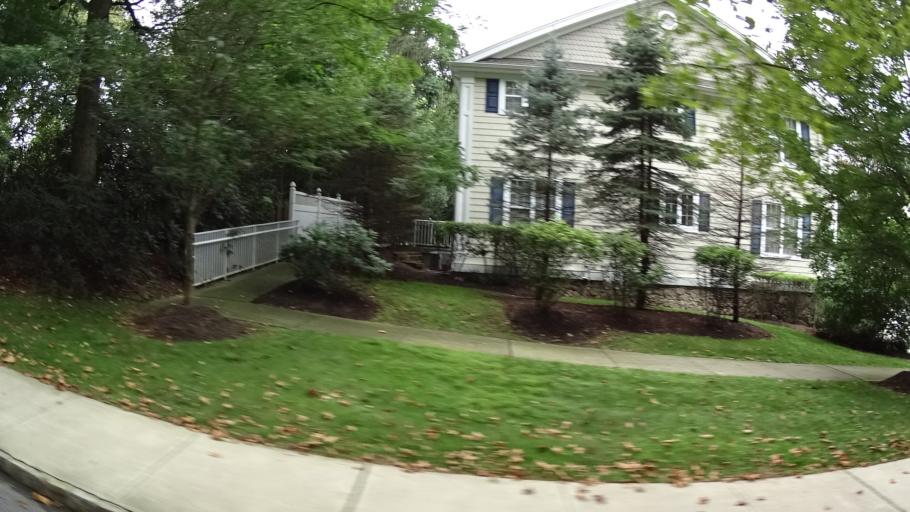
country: US
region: New Jersey
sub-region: Union County
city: New Providence
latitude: 40.7091
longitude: -74.3843
